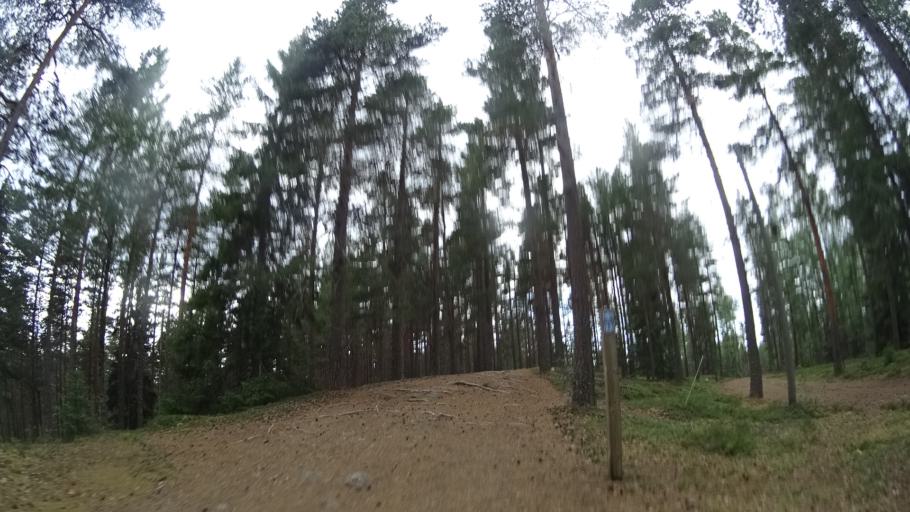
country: FI
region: Satakunta
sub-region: Pohjois-Satakunta
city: Jaemijaervi
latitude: 61.7726
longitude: 22.7345
